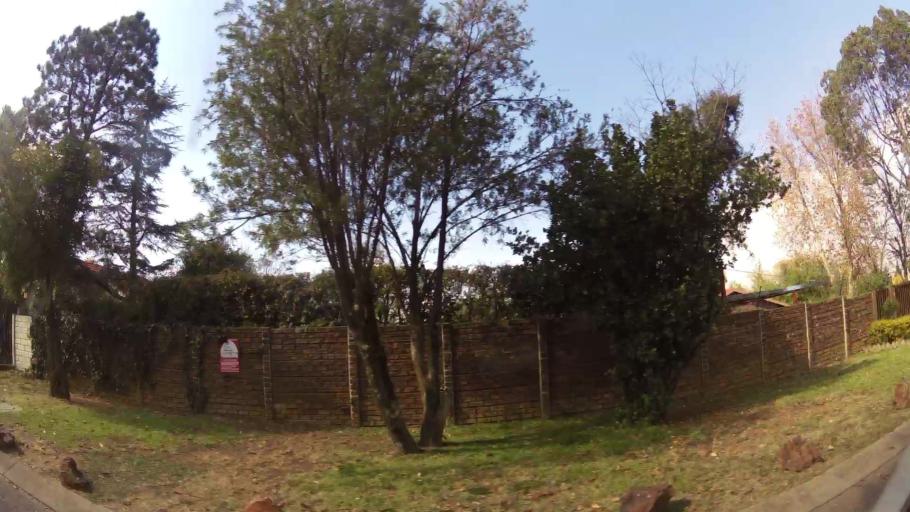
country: ZA
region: Gauteng
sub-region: City of Johannesburg Metropolitan Municipality
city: Midrand
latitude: -25.9982
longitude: 28.1066
